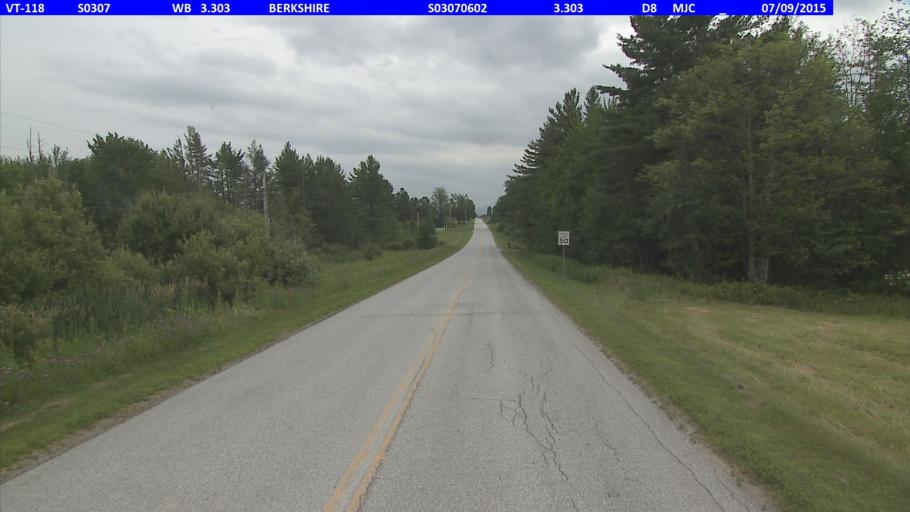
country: US
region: Vermont
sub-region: Franklin County
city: Enosburg Falls
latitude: 44.9630
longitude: -72.7588
